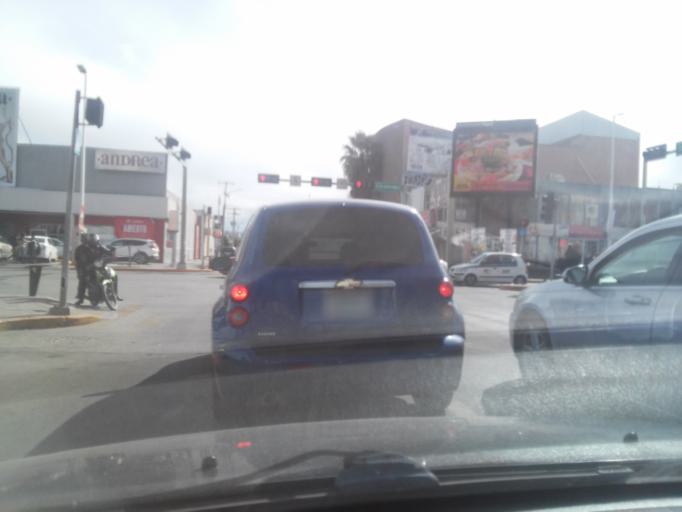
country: MX
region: Durango
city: Victoria de Durango
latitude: 24.0273
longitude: -104.6561
